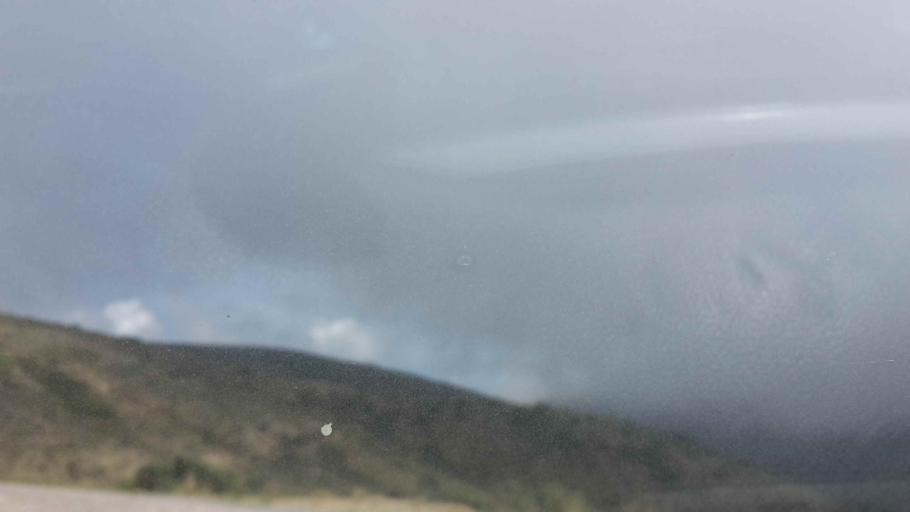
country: BO
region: Cochabamba
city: Cochabamba
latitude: -17.3332
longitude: -66.0712
